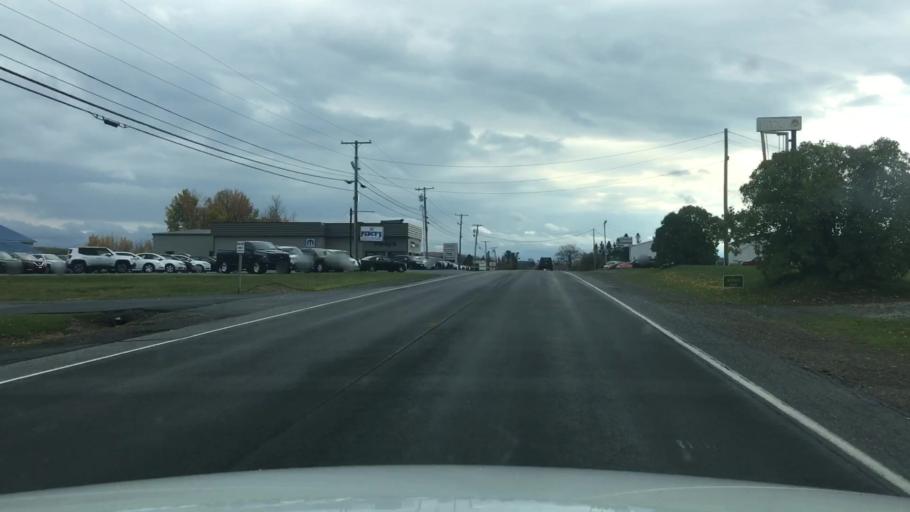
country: US
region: Maine
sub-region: Aroostook County
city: Presque Isle
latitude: 46.6593
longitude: -68.0075
